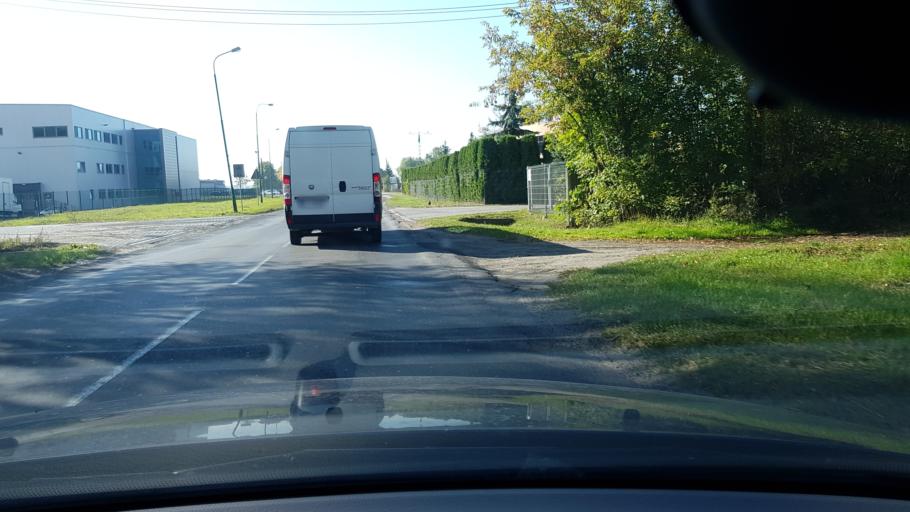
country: PL
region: Lodz Voivodeship
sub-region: Powiat tomaszowski
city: Tomaszow Mazowiecki
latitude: 51.5603
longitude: 20.0207
